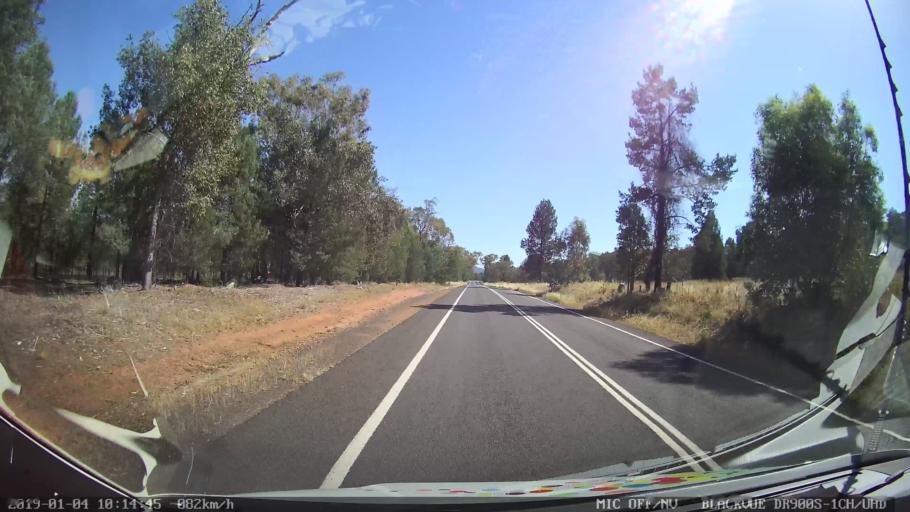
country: AU
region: New South Wales
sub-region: Cabonne
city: Canowindra
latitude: -33.3935
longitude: 148.4156
